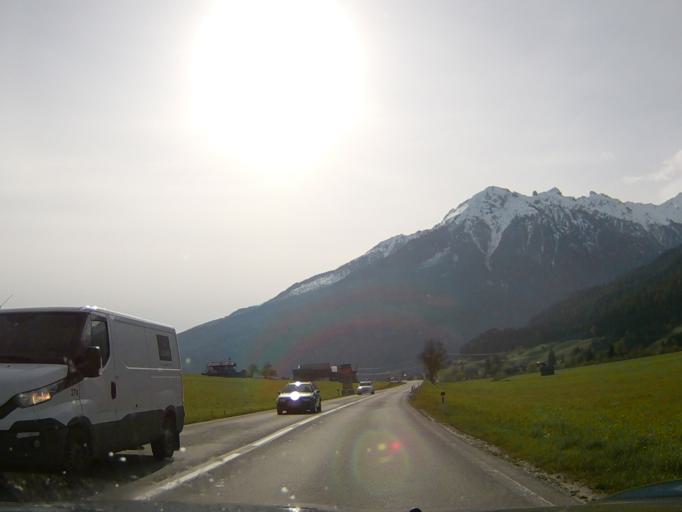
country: AT
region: Salzburg
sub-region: Politischer Bezirk Zell am See
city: Neukirchen am Grossvenediger
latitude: 47.2545
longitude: 12.2831
